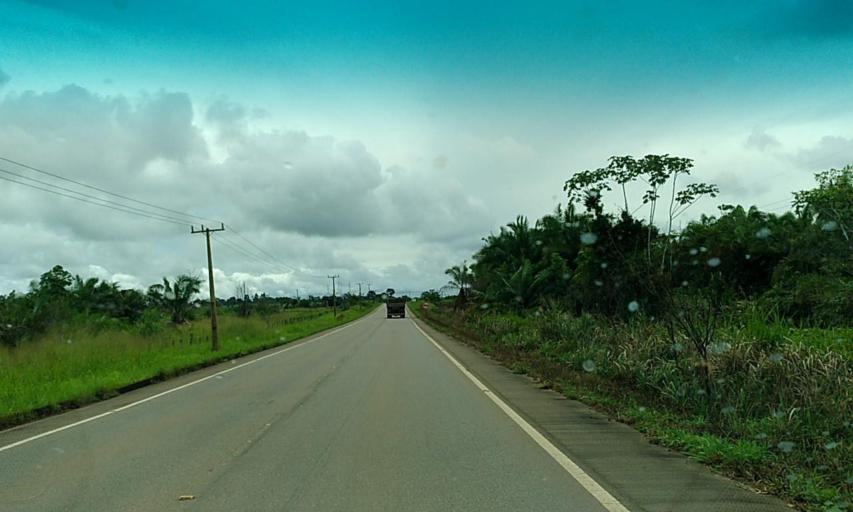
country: BR
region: Para
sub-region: Altamira
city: Altamira
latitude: -3.1095
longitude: -51.6609
